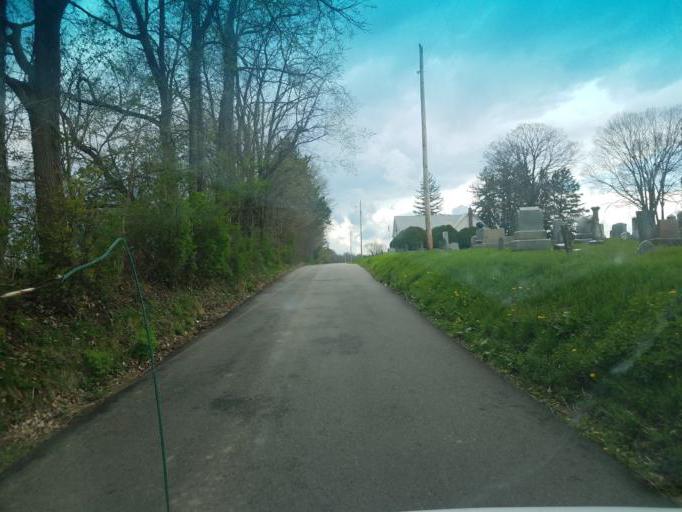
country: US
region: Ohio
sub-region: Knox County
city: Fredericktown
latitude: 40.5378
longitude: -82.5006
